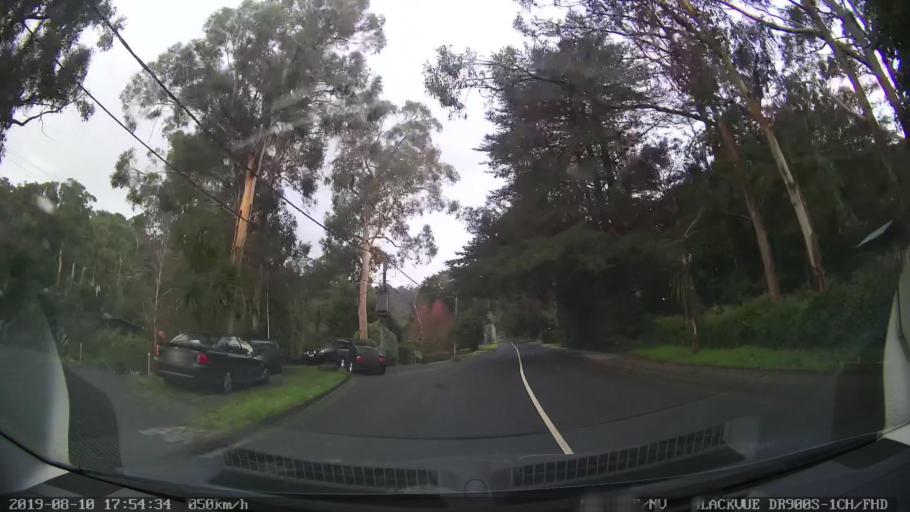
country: AU
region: Victoria
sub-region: Yarra Ranges
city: Tremont
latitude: -37.8992
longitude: 145.3326
